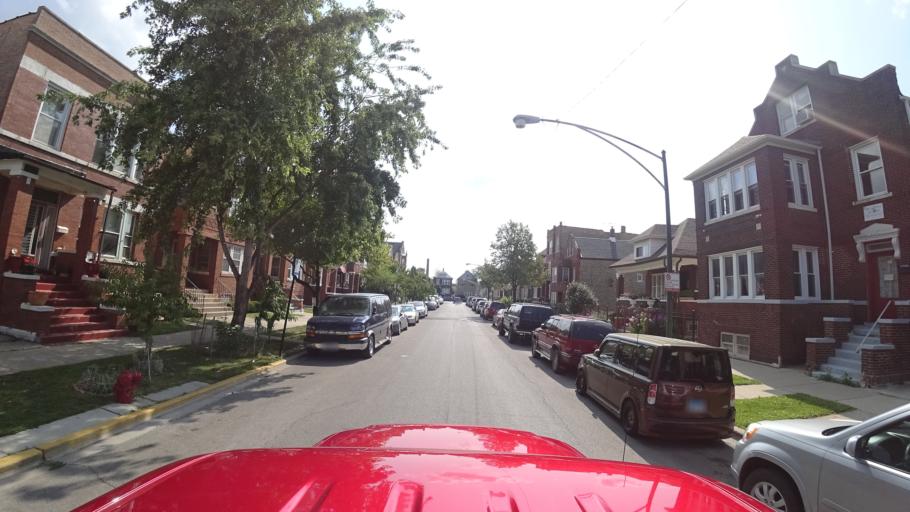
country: US
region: Illinois
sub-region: Cook County
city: Cicero
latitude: 41.8182
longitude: -87.7010
